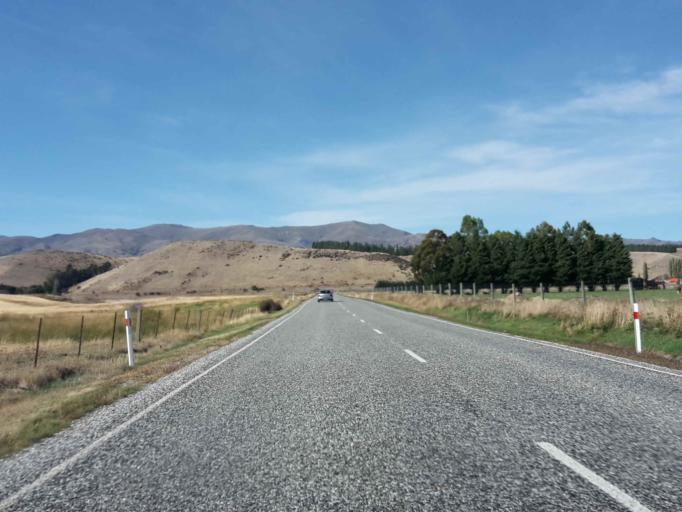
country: NZ
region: Otago
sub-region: Queenstown-Lakes District
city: Wanaka
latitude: -44.8371
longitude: 169.3874
